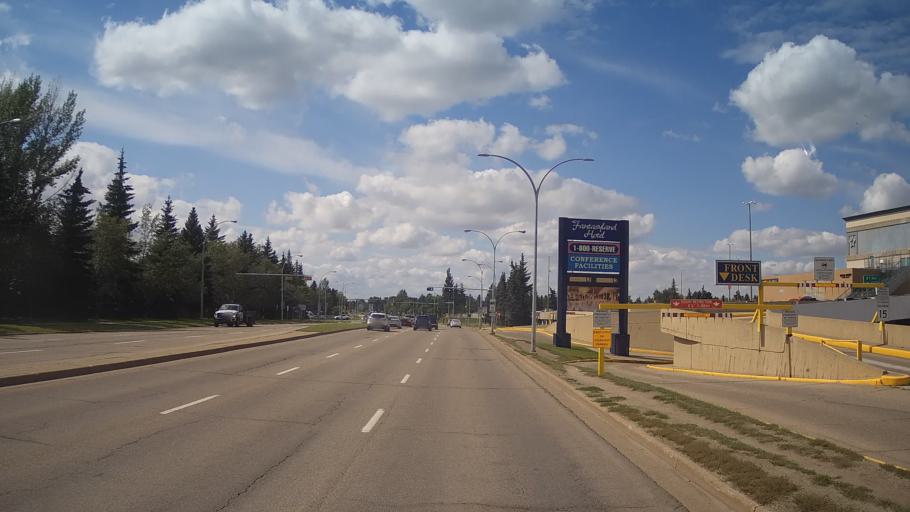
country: CA
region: Alberta
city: St. Albert
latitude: 53.5209
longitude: -113.6269
